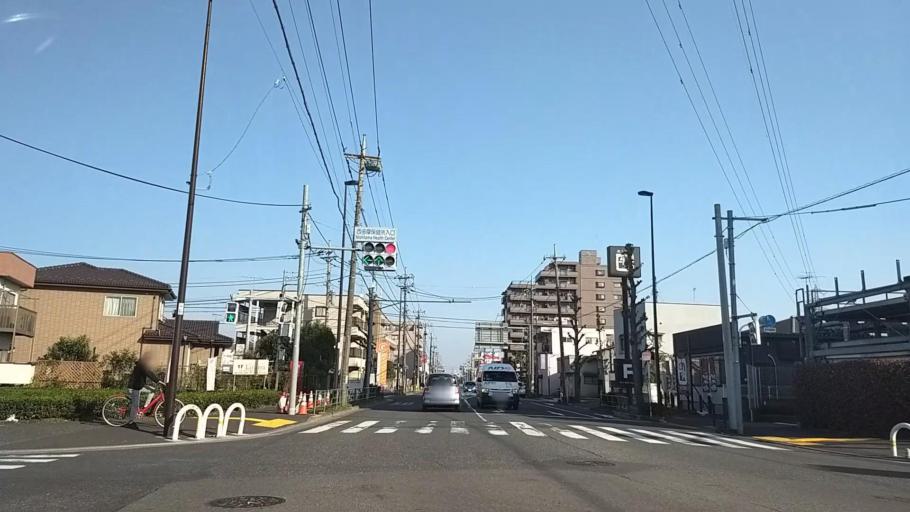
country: JP
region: Tokyo
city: Ome
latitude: 35.7889
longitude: 139.2821
